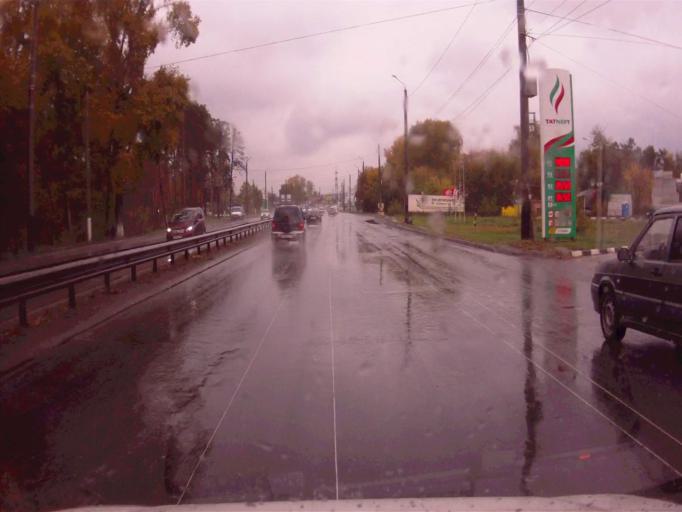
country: RU
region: Chelyabinsk
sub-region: Gorod Chelyabinsk
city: Chelyabinsk
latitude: 55.2348
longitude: 61.3661
